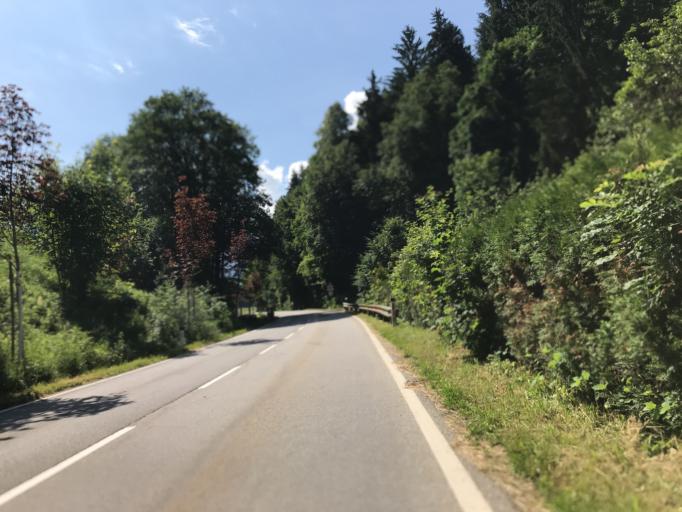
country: AT
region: Carinthia
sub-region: Villach Stadt
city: Villach
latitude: 46.5819
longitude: 13.8291
